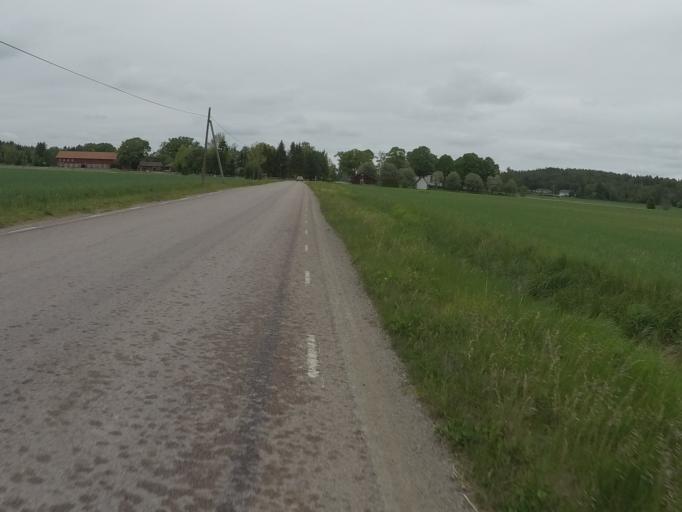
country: SE
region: Vaestmanland
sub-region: Hallstahammars Kommun
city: Kolback
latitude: 59.5455
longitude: 16.3108
